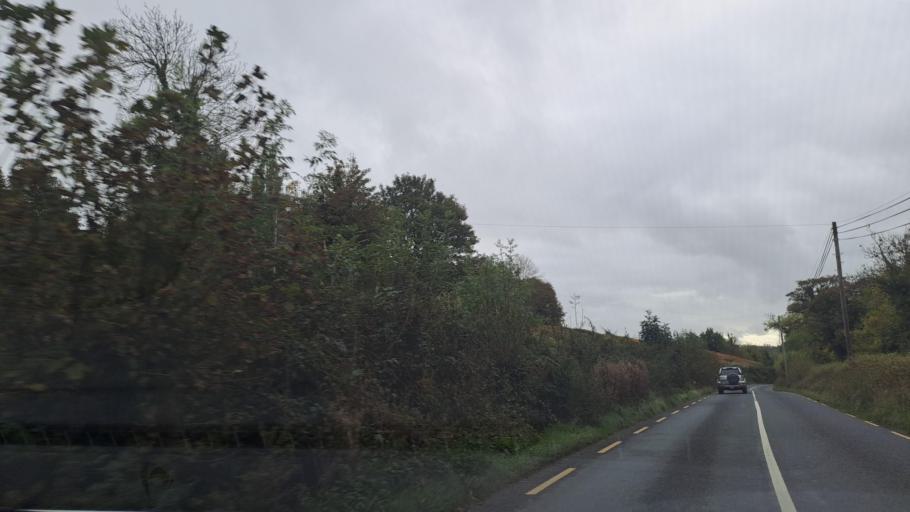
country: IE
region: Ulster
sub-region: An Cabhan
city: Cootehill
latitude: 54.0648
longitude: -7.0605
